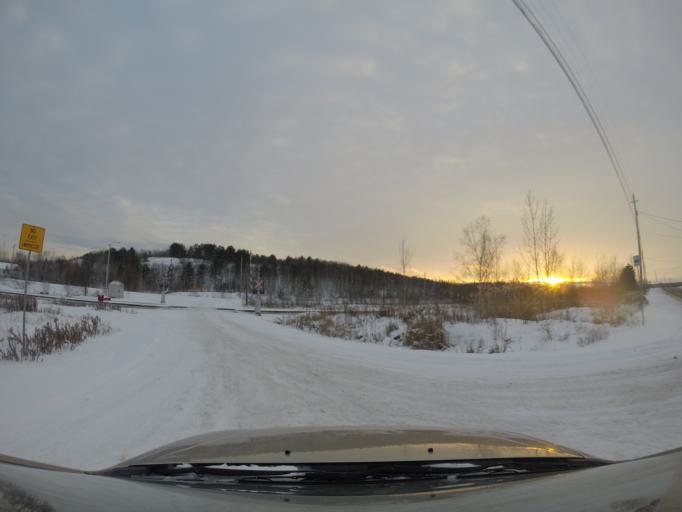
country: CA
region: Ontario
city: Greater Sudbury
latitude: 46.4856
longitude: -80.8741
